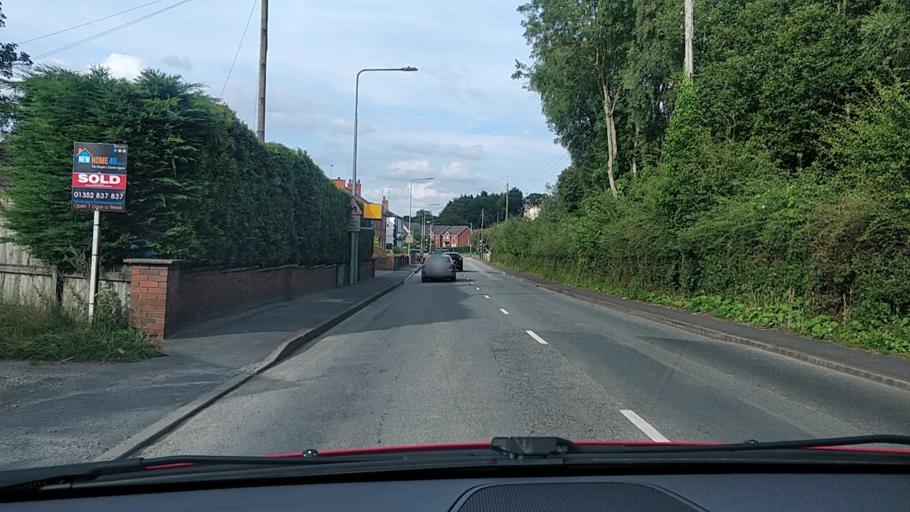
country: GB
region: Wales
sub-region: County of Flintshire
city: Leeswood
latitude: 53.1235
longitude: -3.0930
